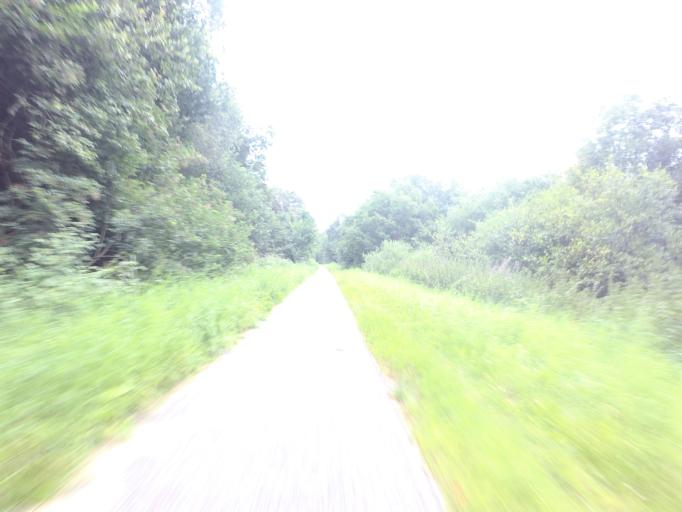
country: DK
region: Central Jutland
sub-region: Horsens Kommune
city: Braedstrup
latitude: 56.0225
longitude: 9.5358
